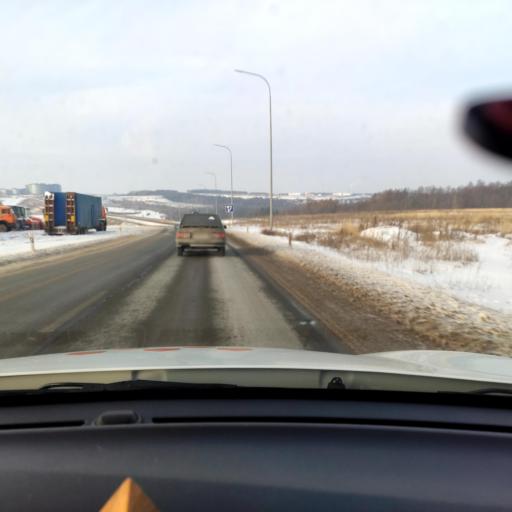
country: RU
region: Tatarstan
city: Sviyazhsk
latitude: 55.7422
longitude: 48.7761
